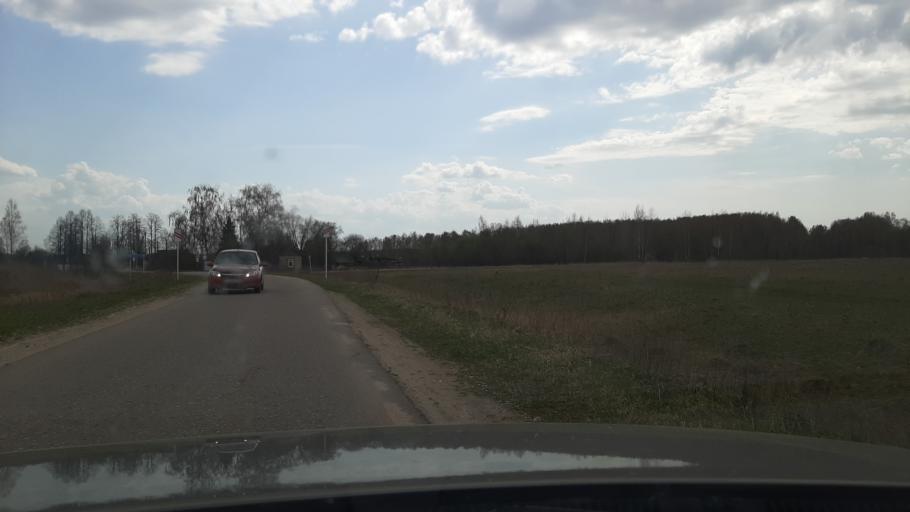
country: RU
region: Ivanovo
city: Furmanov
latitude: 57.3042
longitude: 41.1616
